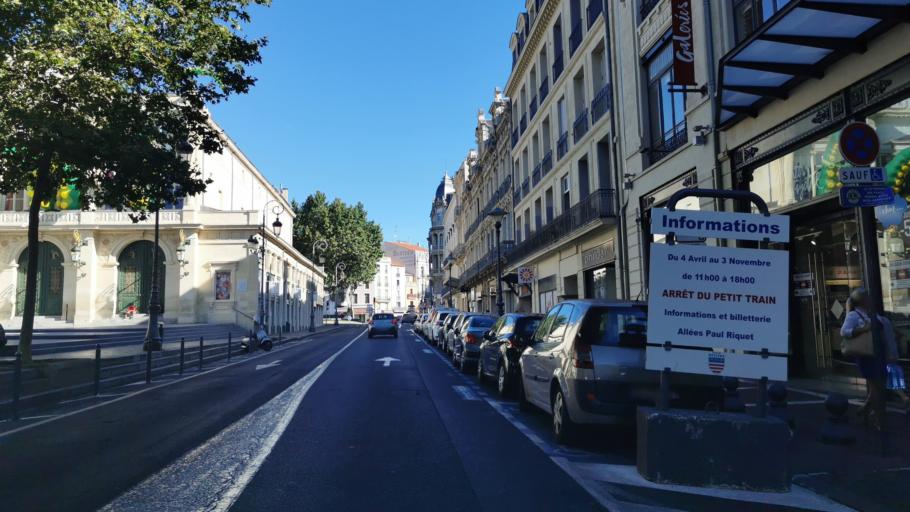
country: FR
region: Languedoc-Roussillon
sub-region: Departement de l'Herault
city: Beziers
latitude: 43.3439
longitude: 3.2164
